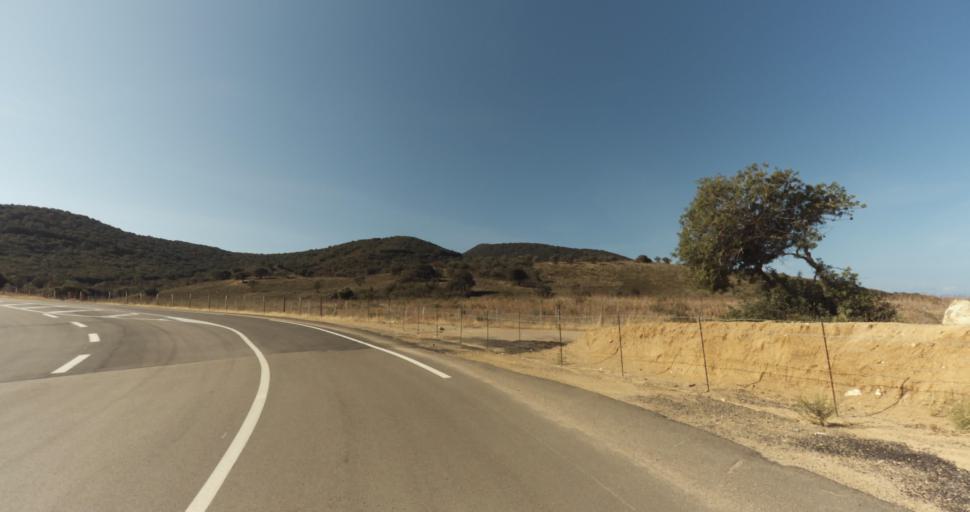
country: FR
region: Corsica
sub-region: Departement de la Corse-du-Sud
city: Ajaccio
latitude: 41.9300
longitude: 8.6481
